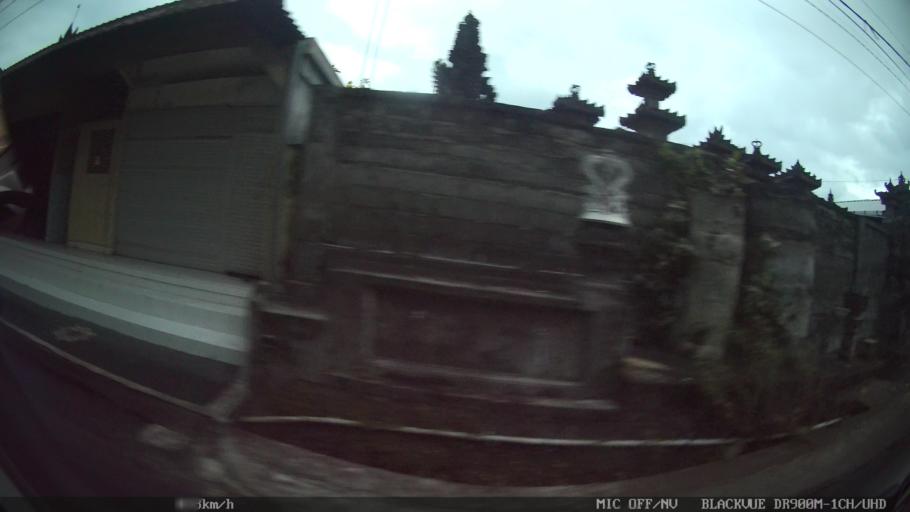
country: ID
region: Bali
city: Banjar Pasekan
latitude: -8.6142
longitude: 115.2860
